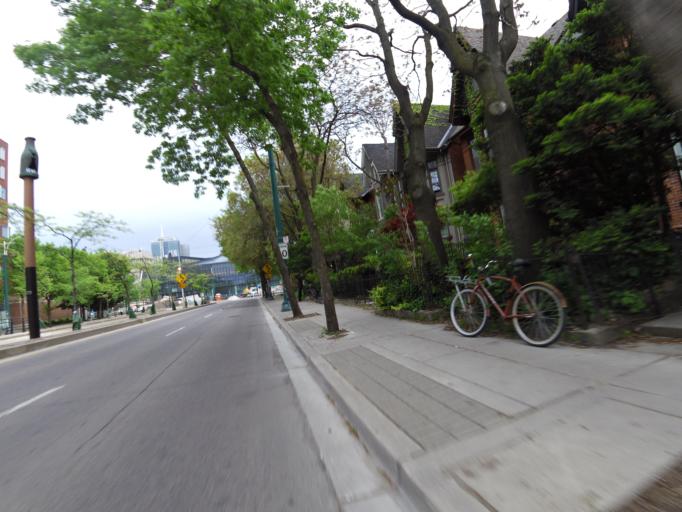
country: CA
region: Ontario
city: Toronto
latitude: 43.6611
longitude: -79.4015
